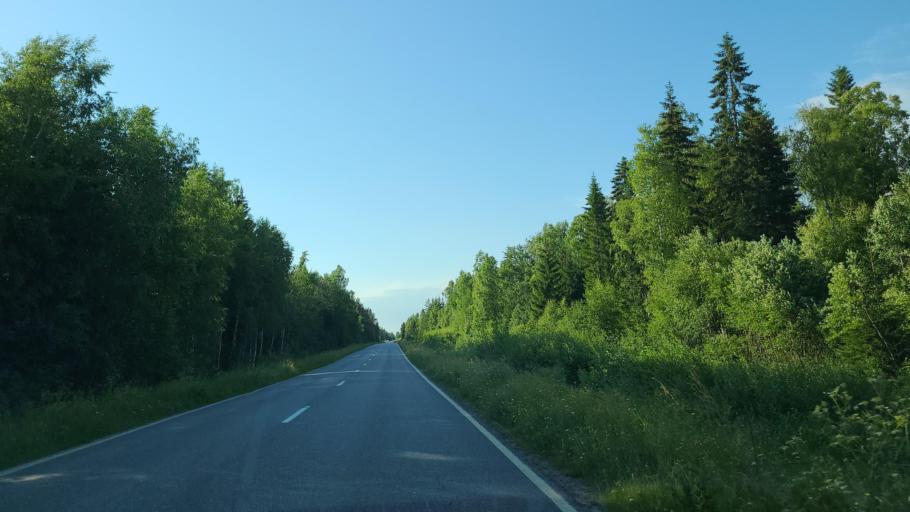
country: FI
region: Ostrobothnia
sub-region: Vaasa
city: Replot
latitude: 63.2518
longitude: 21.3727
